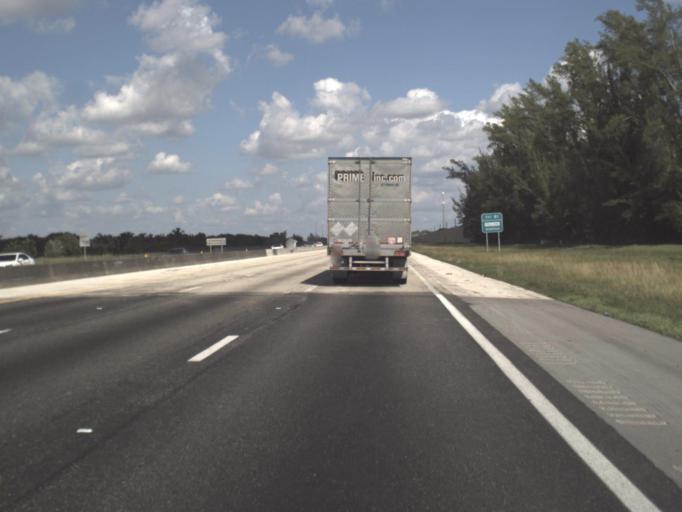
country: US
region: Florida
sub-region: Palm Beach County
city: Villages of Oriole
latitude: 26.4428
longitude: -80.1742
